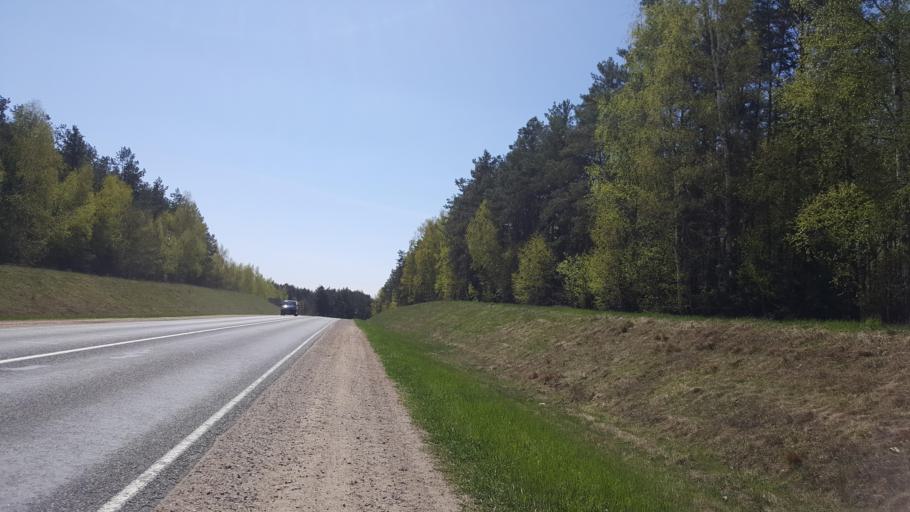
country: BY
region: Brest
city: Kamyanyets
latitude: 52.3472
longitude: 23.7787
